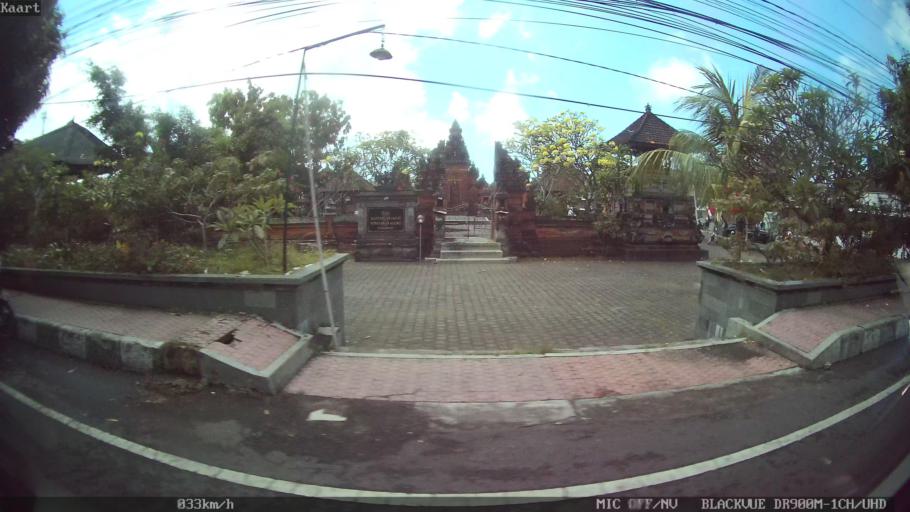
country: ID
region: Bali
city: Banjar Pasekan
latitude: -8.5932
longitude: 115.2828
